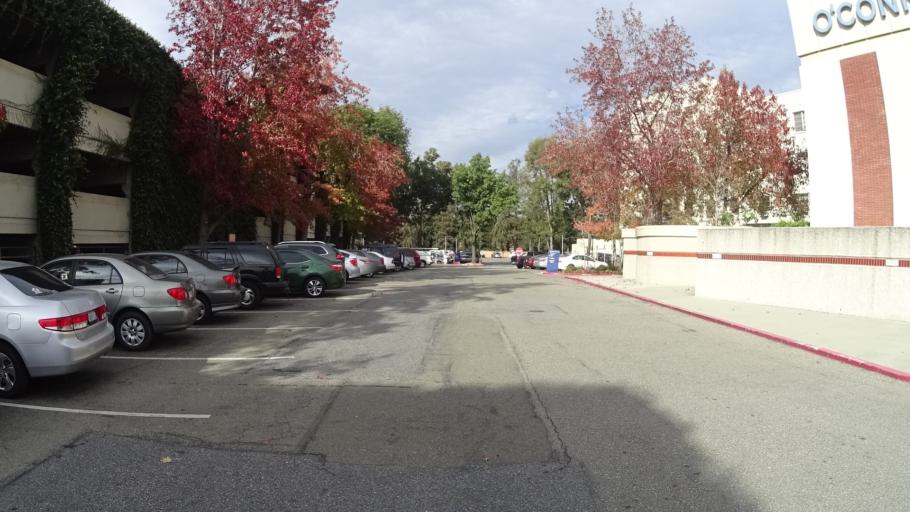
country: US
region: California
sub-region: Santa Clara County
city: Burbank
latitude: 37.3277
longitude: -121.9397
